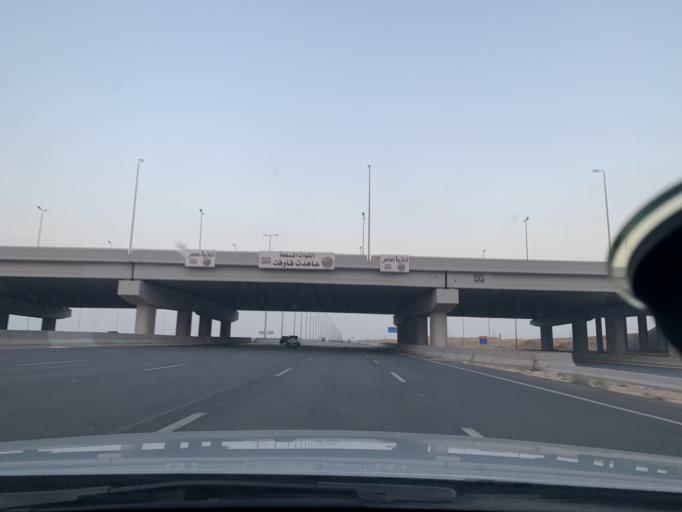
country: EG
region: Muhafazat al Qalyubiyah
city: Al Khankah
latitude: 30.0907
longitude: 31.5053
